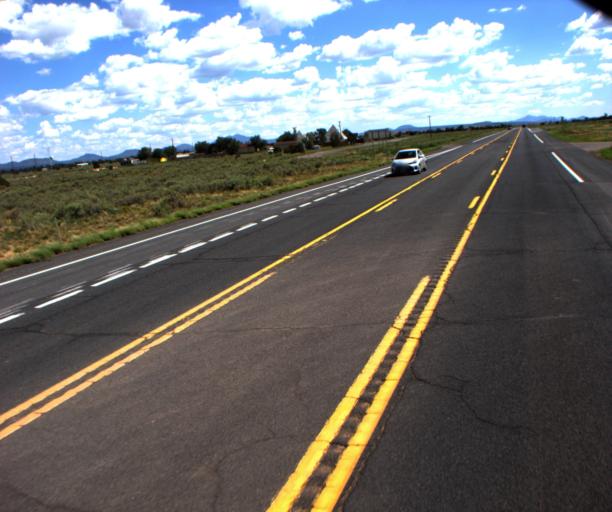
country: US
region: Arizona
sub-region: Coconino County
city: Grand Canyon Village
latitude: 35.6515
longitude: -112.1396
